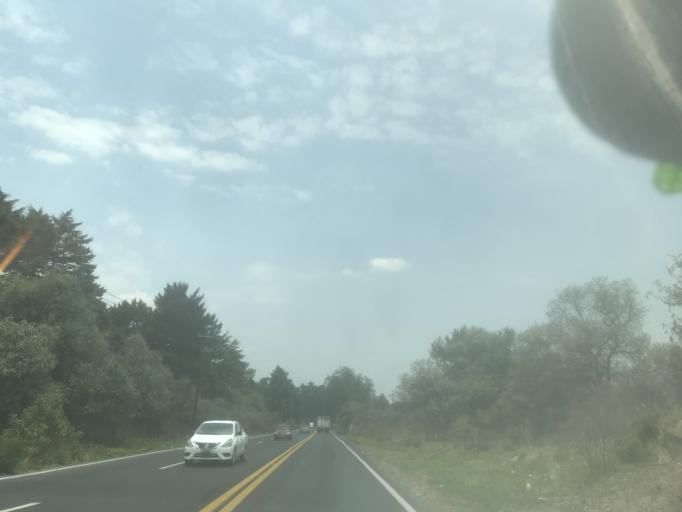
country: MX
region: Mexico
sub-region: Amecameca
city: San Diego Huehuecalco
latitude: 19.0782
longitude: -98.7816
